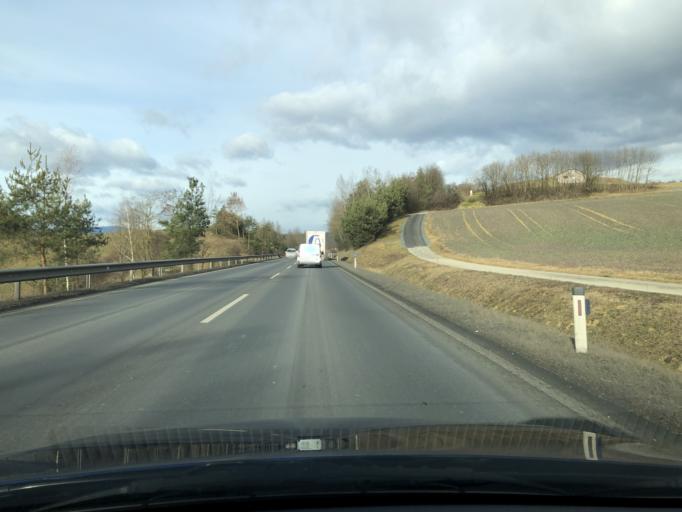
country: AT
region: Burgenland
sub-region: Politischer Bezirk Oberwart
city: Oberwart
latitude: 47.2766
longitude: 16.1969
